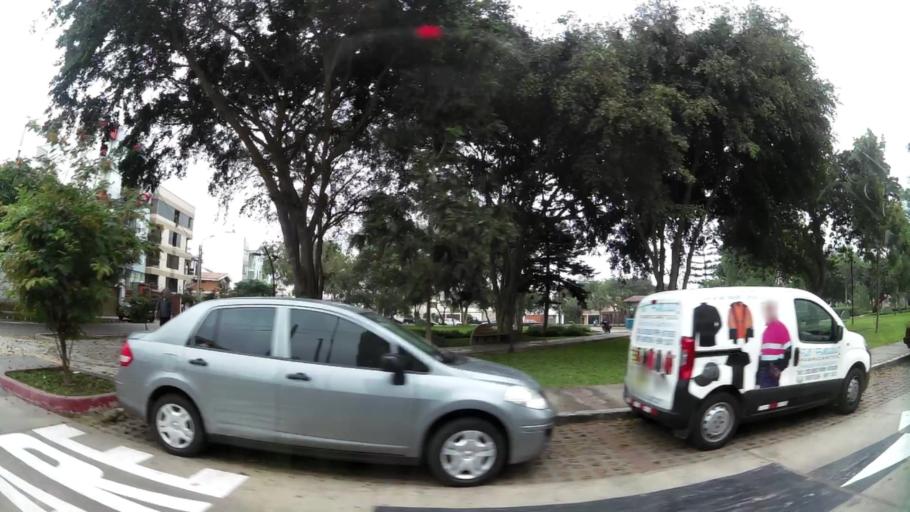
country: PE
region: Lima
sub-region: Lima
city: San Luis
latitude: -12.1032
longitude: -77.0024
